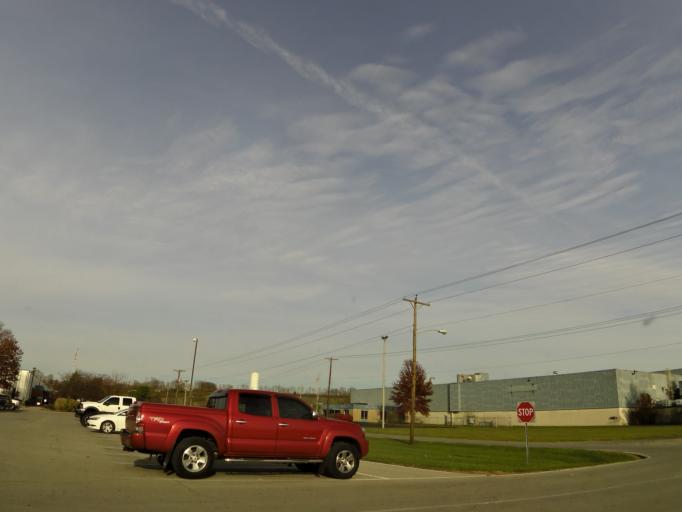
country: US
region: Kentucky
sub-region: Harrison County
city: Cynthiana
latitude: 38.3723
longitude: -84.2940
